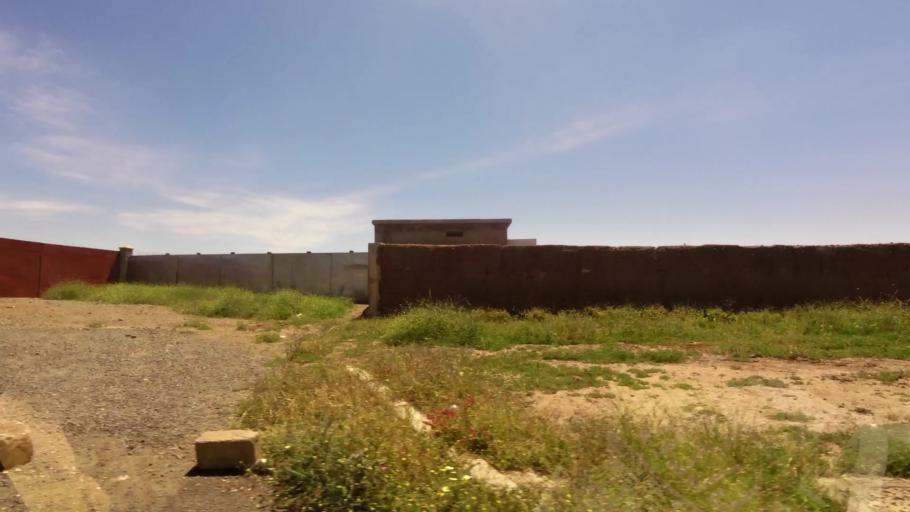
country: MA
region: Marrakech-Tensift-Al Haouz
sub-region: Marrakech
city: Marrakesh
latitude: 31.6248
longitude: -8.0203
